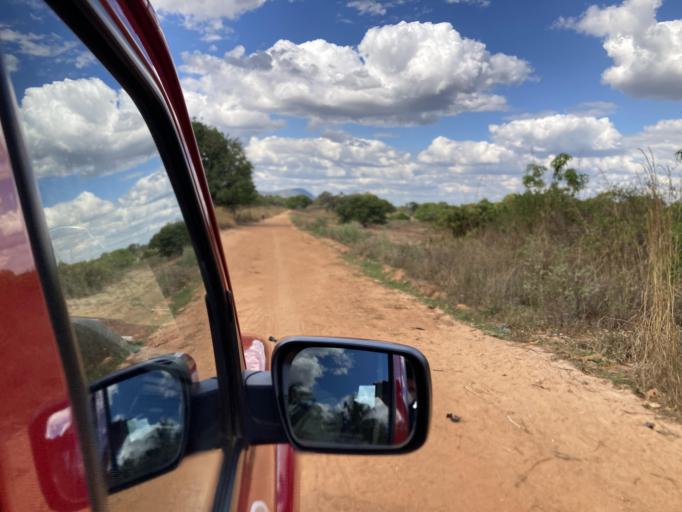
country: MZ
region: Cabo Delgado
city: Montepuez
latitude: -13.1264
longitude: 39.0387
